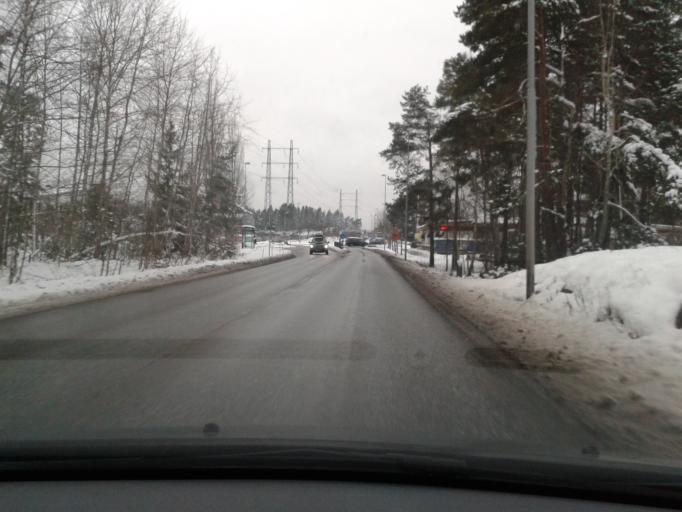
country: SE
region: Stockholm
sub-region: Tyreso Kommun
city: Bollmora
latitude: 59.2469
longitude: 18.2497
